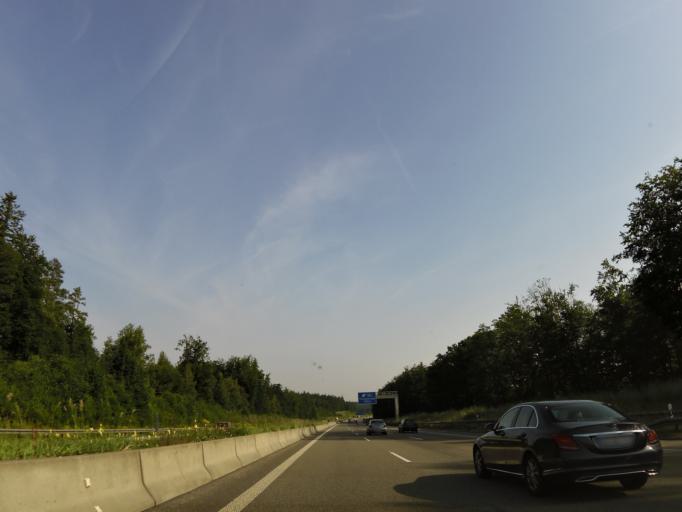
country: DE
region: Baden-Wuerttemberg
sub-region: Karlsruhe Region
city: Wurmberg
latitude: 48.8672
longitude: 8.7916
